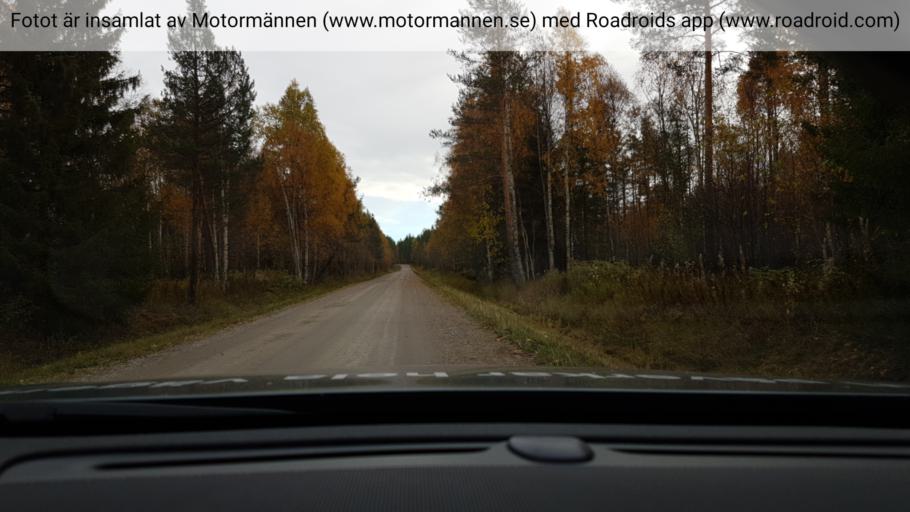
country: SE
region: Norrbotten
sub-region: Overkalix Kommun
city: OEverkalix
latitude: 66.2942
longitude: 22.9480
